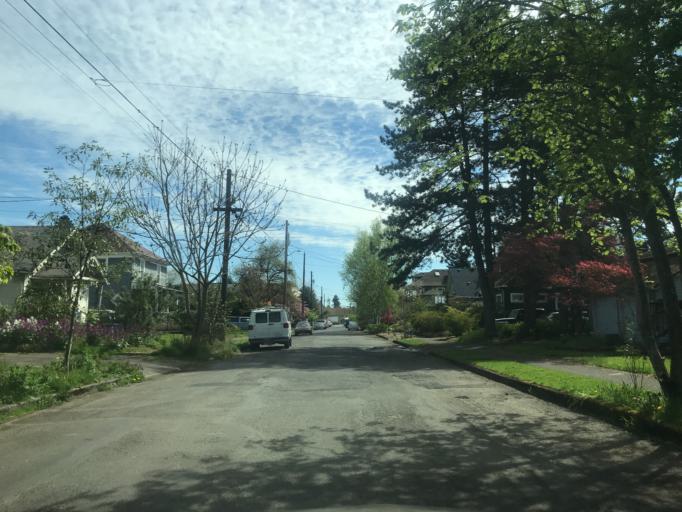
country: US
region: Oregon
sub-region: Multnomah County
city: Lents
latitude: 45.4864
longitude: -122.5930
